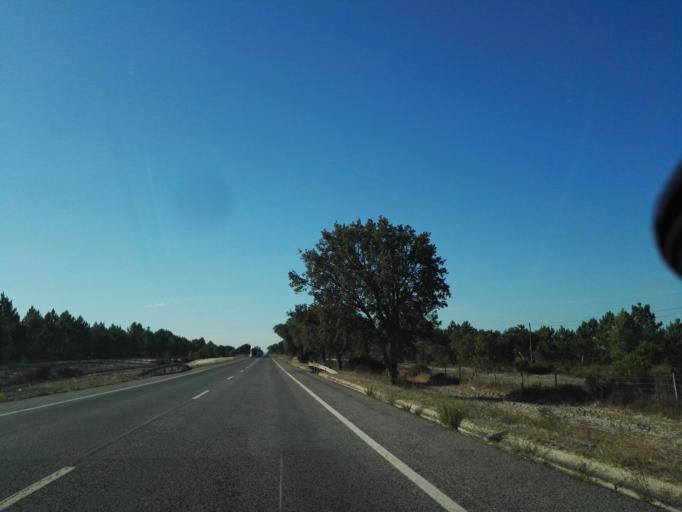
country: PT
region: Santarem
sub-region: Benavente
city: Poceirao
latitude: 38.8796
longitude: -8.8131
